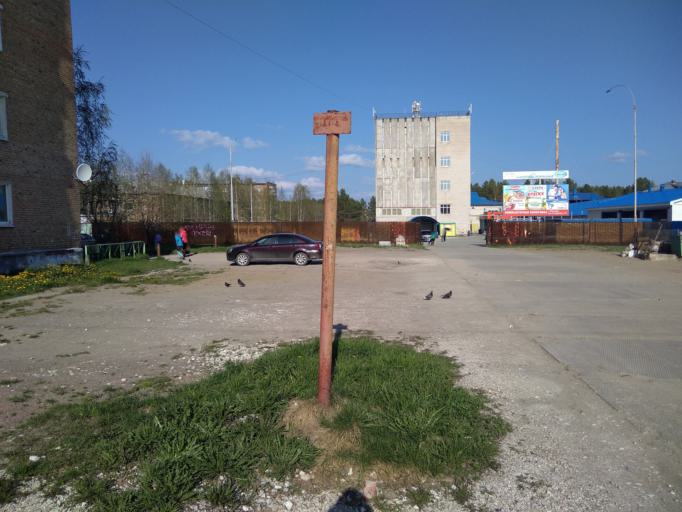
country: RU
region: Komi Republic
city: Pechora
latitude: 65.1255
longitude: 57.1543
